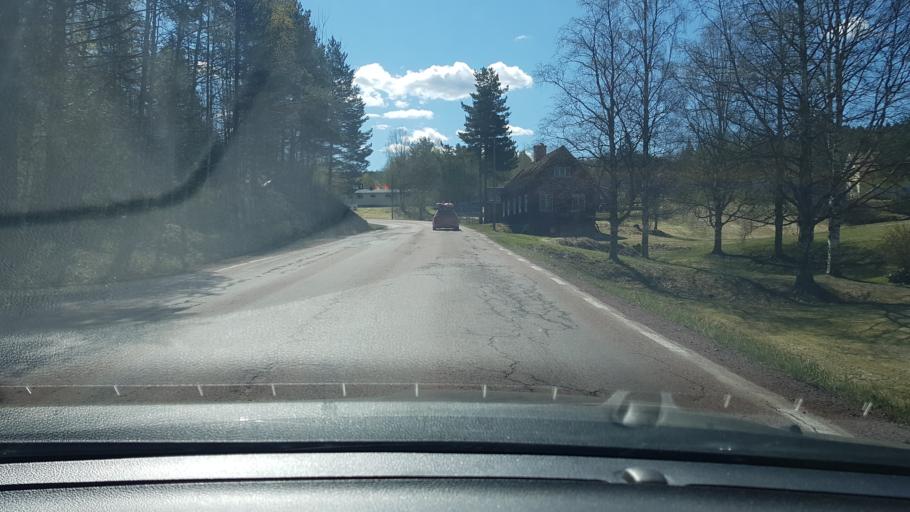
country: SE
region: Dalarna
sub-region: Alvdalens Kommun
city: AElvdalen
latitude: 61.1183
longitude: 14.1712
